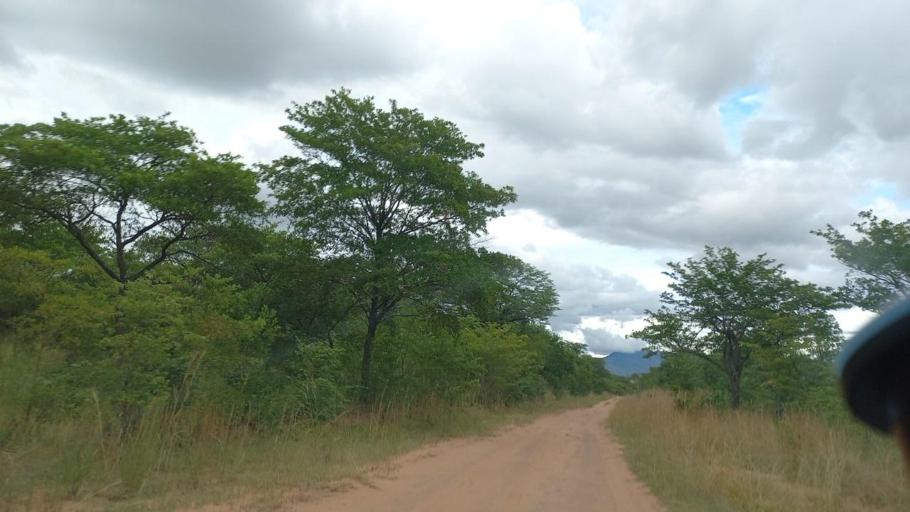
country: ZM
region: Lusaka
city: Luangwa
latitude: -15.5629
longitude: 30.3288
